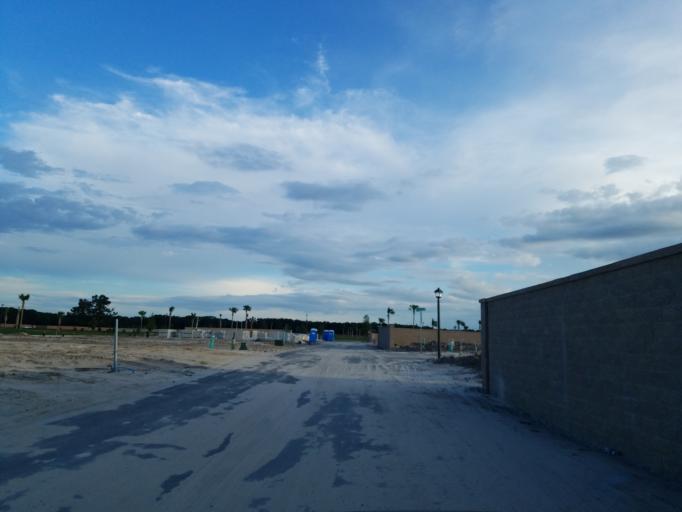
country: US
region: Florida
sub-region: Sumter County
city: Wildwood
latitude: 28.7913
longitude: -82.0109
